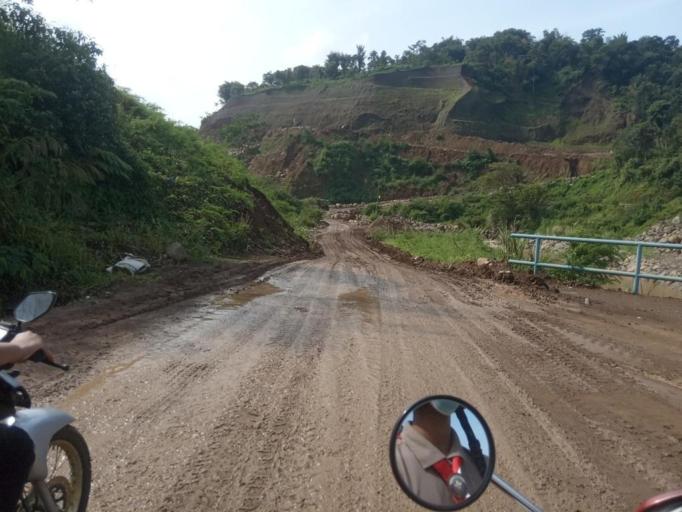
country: ID
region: West Java
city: Caringin
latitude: -6.6579
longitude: 106.8830
